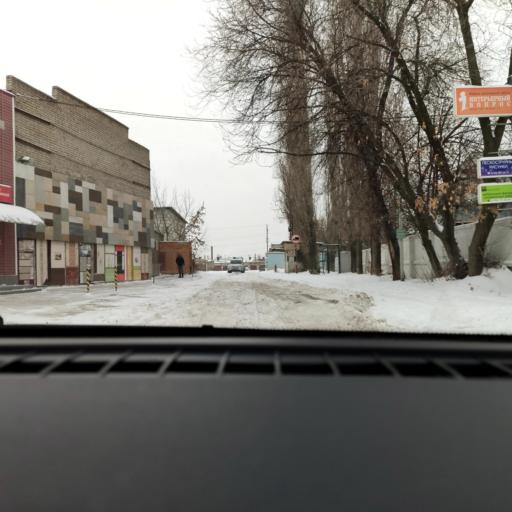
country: RU
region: Voronezj
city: Voronezh
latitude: 51.6340
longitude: 39.2507
